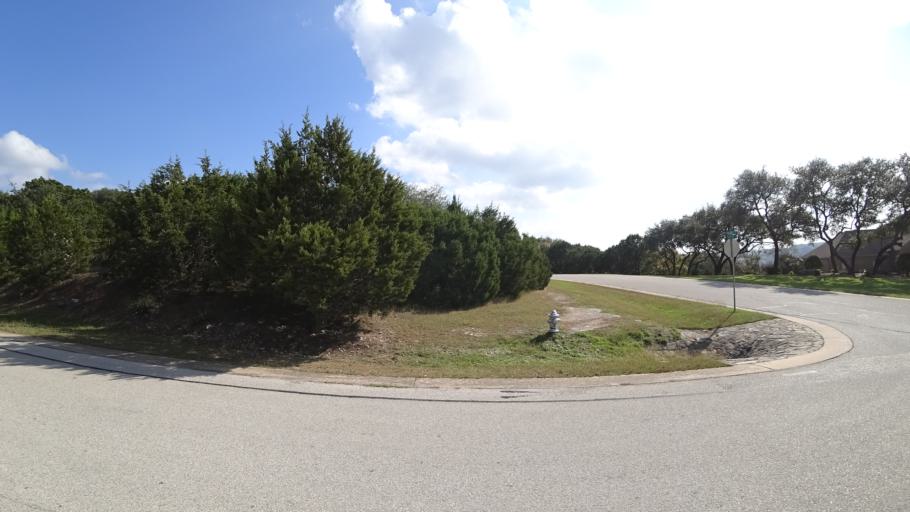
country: US
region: Texas
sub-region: Travis County
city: Lost Creek
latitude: 30.3084
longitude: -97.8554
